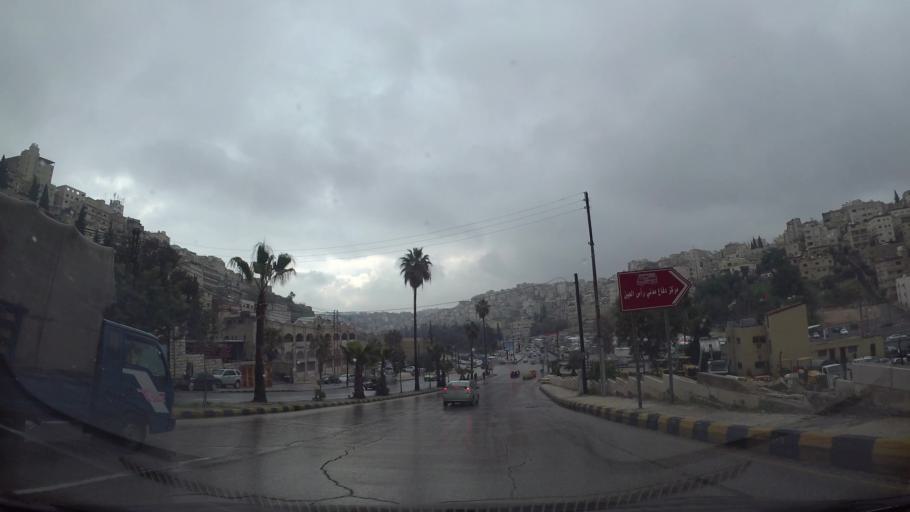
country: JO
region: Amman
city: Amman
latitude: 31.9491
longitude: 35.9147
